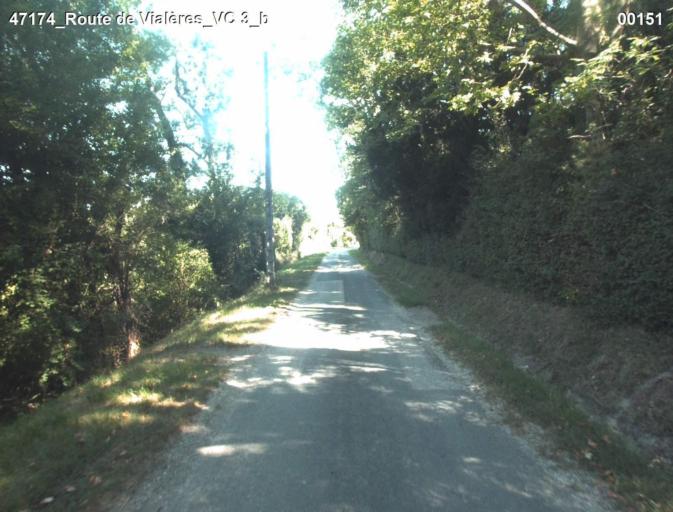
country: FR
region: Midi-Pyrenees
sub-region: Departement du Gers
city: Condom
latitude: 44.0371
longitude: 0.3700
